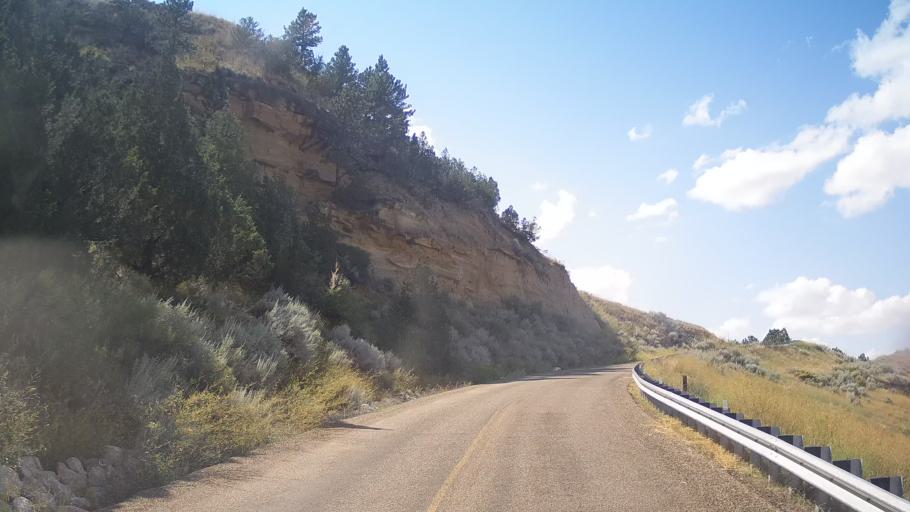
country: US
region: Montana
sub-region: Dawson County
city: Glendive
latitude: 47.0620
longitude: -104.6810
